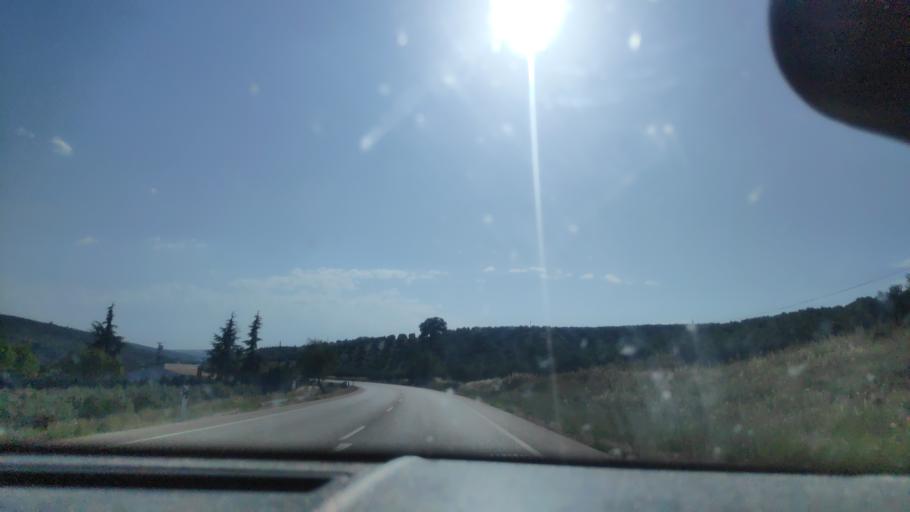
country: ES
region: Andalusia
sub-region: Provincia de Granada
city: Benalua de las Villas
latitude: 37.4390
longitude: -3.6591
